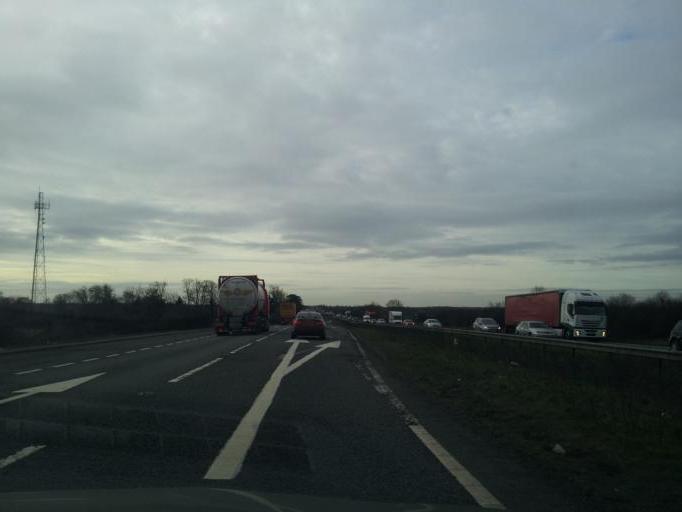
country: GB
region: England
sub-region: District of Rutland
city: Clipsham
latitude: 52.7836
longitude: -0.6108
